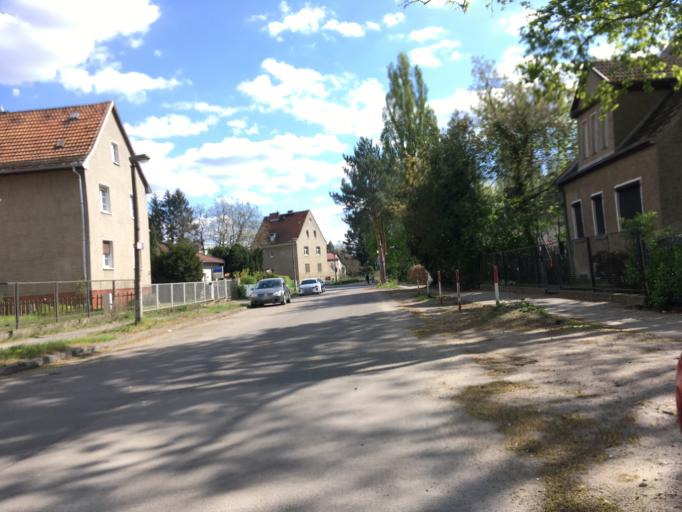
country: DE
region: Berlin
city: Mahlsdorf
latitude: 52.5105
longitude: 13.6151
